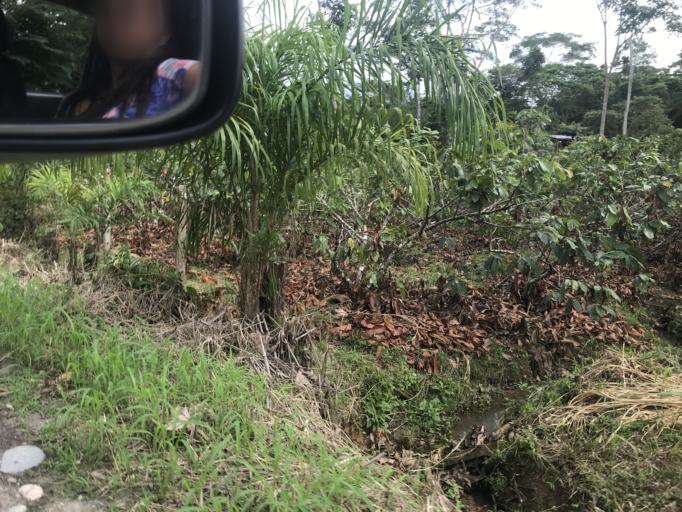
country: EC
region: Napo
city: Tena
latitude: -1.0531
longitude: -77.7728
